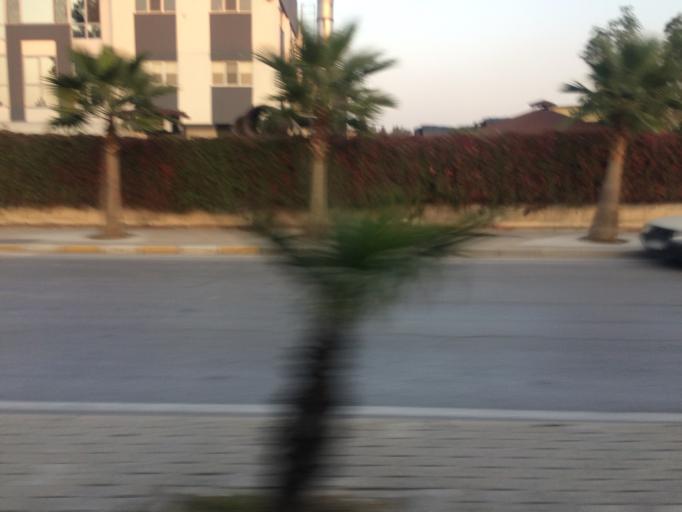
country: TR
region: Izmir
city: Karsiyaka
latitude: 38.4962
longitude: 27.0371
